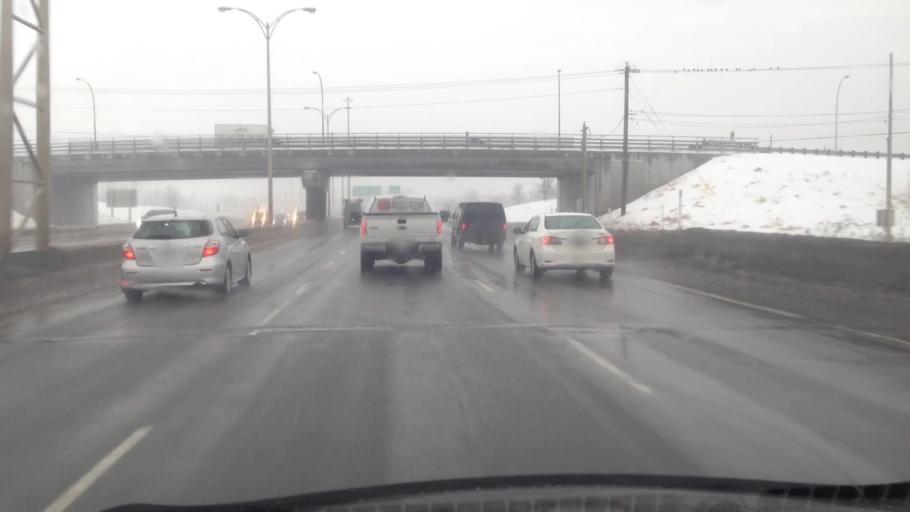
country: CA
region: Quebec
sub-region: Laurentides
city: Boisbriand
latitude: 45.6146
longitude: -73.8191
